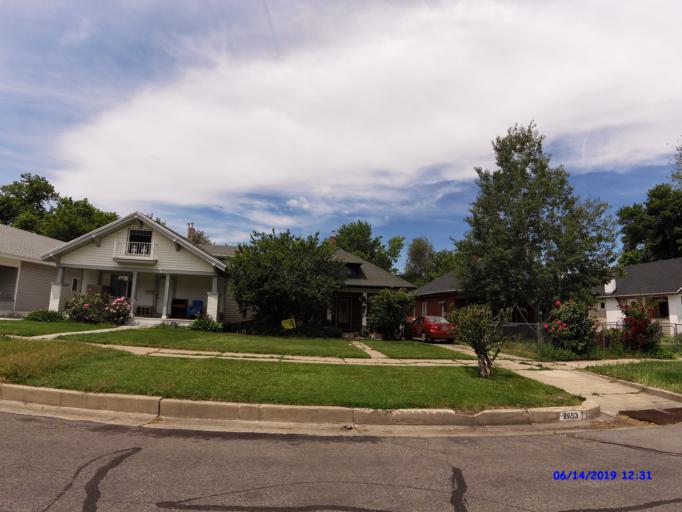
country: US
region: Utah
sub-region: Weber County
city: Ogden
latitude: 41.2171
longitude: -111.9511
